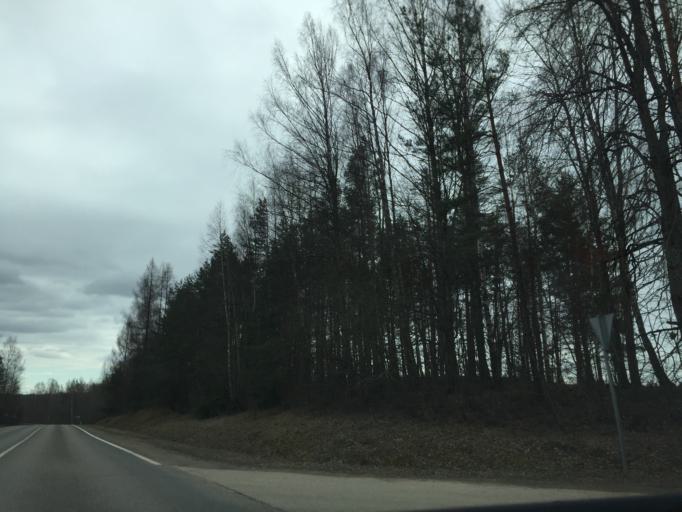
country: LV
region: Kraslavas Rajons
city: Kraslava
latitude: 55.8969
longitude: 27.1257
